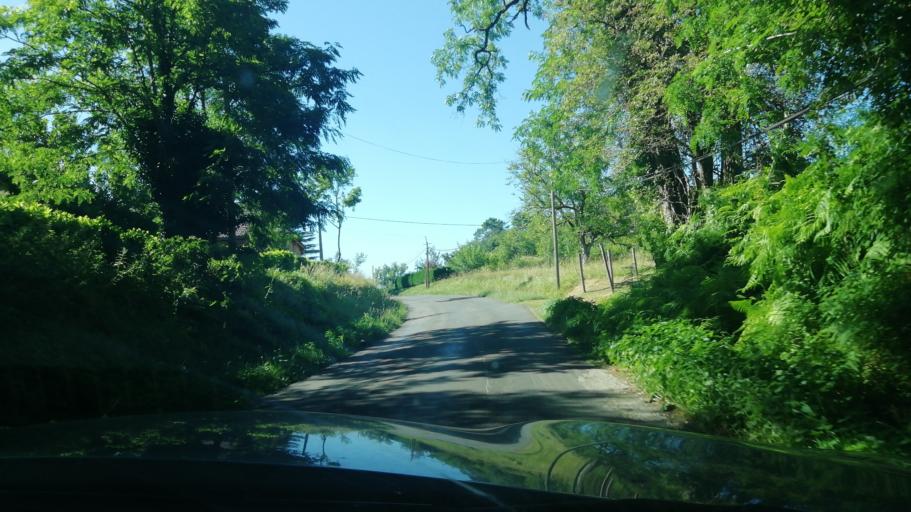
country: FR
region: Aquitaine
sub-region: Departement de la Dordogne
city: Sarlat-la-Caneda
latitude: 44.8630
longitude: 1.2238
